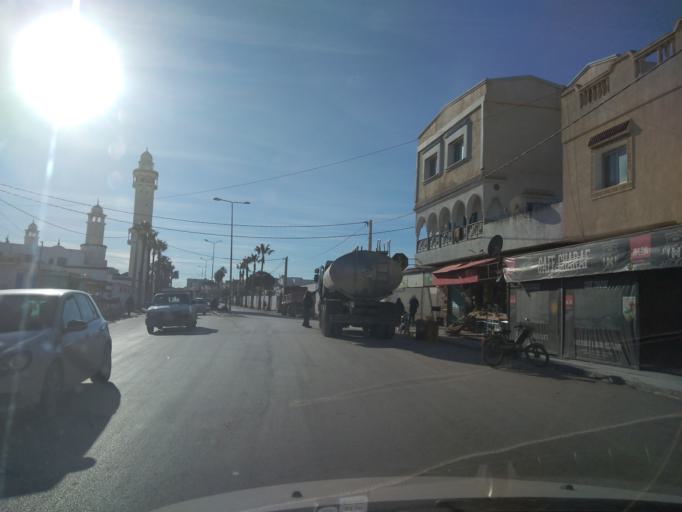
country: TN
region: Ariana
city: Qal'at al Andalus
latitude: 37.0600
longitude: 10.1121
